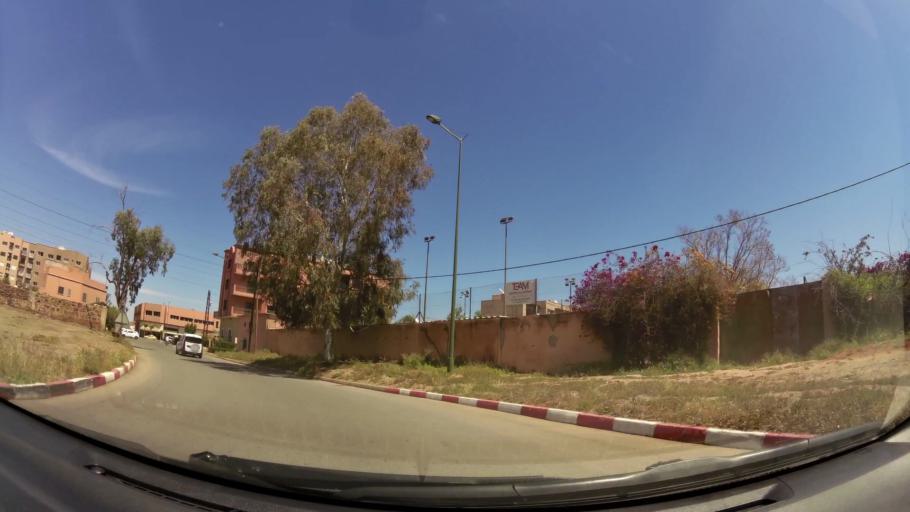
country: MA
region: Marrakech-Tensift-Al Haouz
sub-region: Marrakech
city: Marrakesh
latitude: 31.6249
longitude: -8.0202
